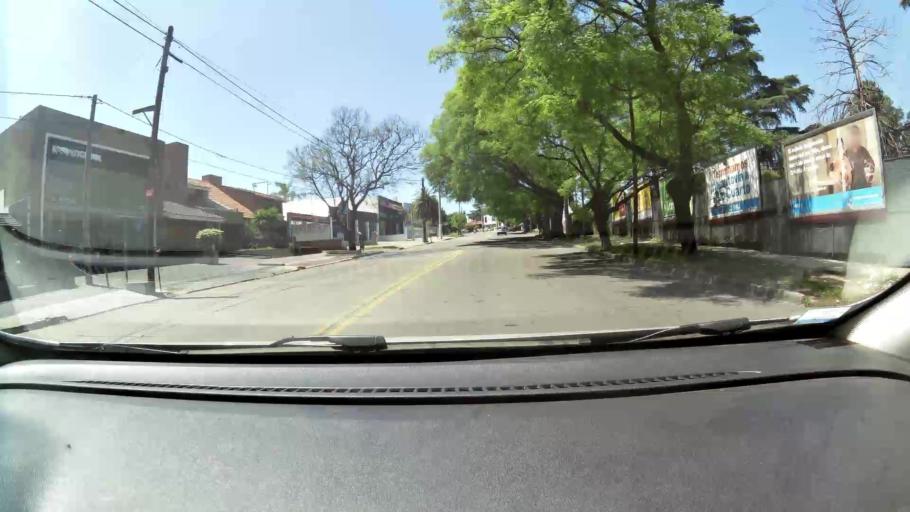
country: AR
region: Cordoba
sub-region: Departamento de Capital
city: Cordoba
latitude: -31.3827
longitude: -64.2076
